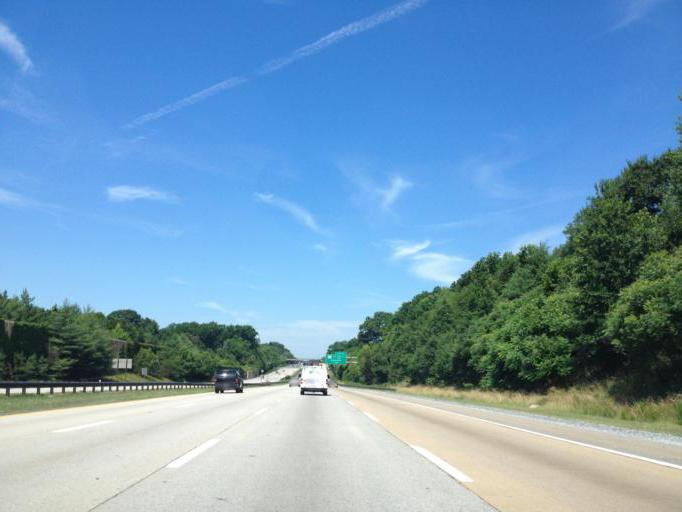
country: US
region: Maryland
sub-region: Prince George's County
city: Springdale
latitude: 38.9467
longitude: -76.8144
